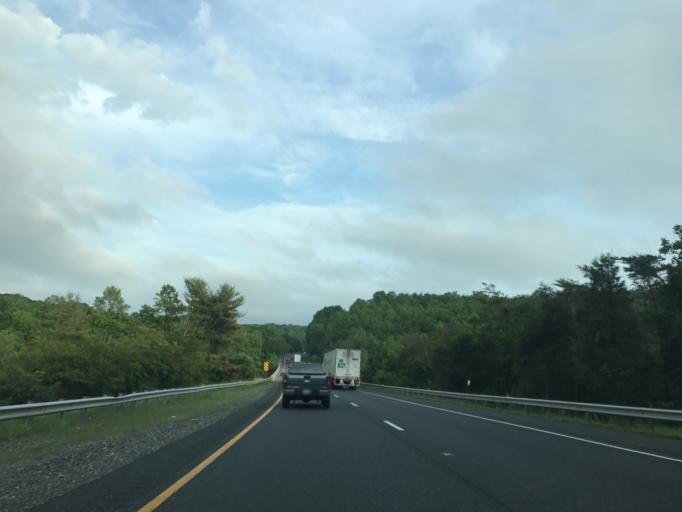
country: US
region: Maryland
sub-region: Baltimore County
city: Hunt Valley
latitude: 39.6144
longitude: -76.6626
